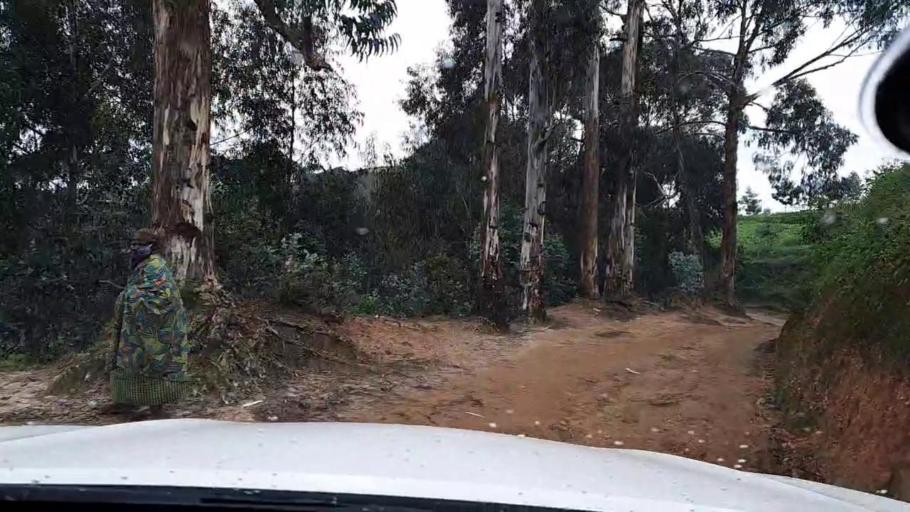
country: RW
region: Southern Province
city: Nzega
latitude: -2.3785
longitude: 29.2462
